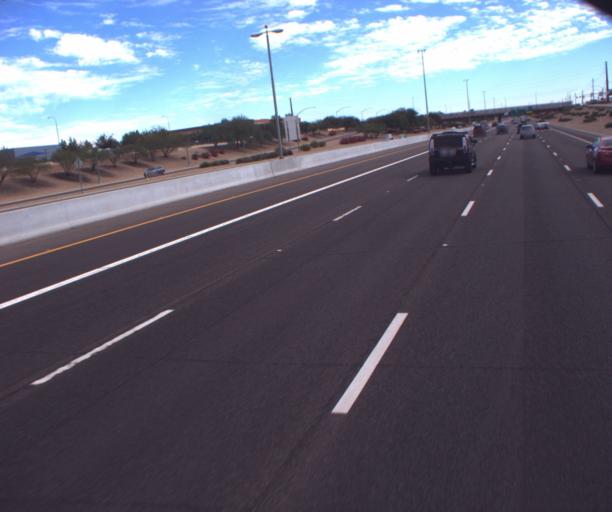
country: US
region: Arizona
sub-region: Maricopa County
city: Chandler
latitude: 33.2915
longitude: -111.9160
